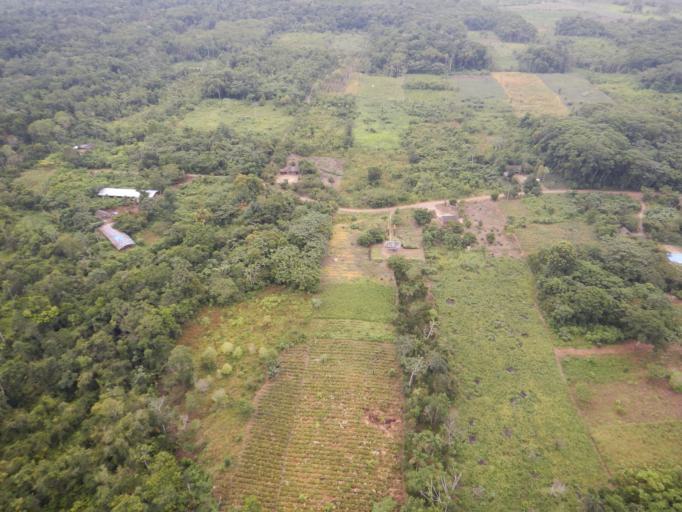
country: BO
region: Cochabamba
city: Chimore
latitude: -17.1045
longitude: -64.8535
